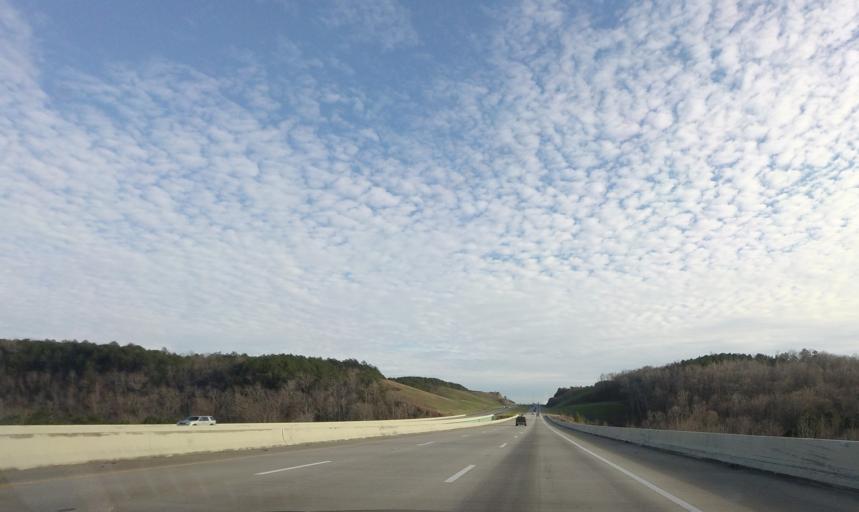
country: US
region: Alabama
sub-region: Walker County
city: Dora
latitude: 33.7085
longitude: -87.1443
